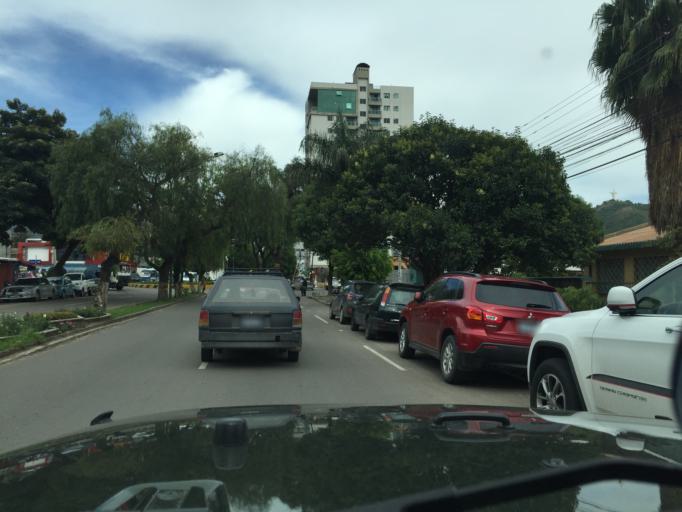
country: BO
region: Cochabamba
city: Cochabamba
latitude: -17.3733
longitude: -66.1503
